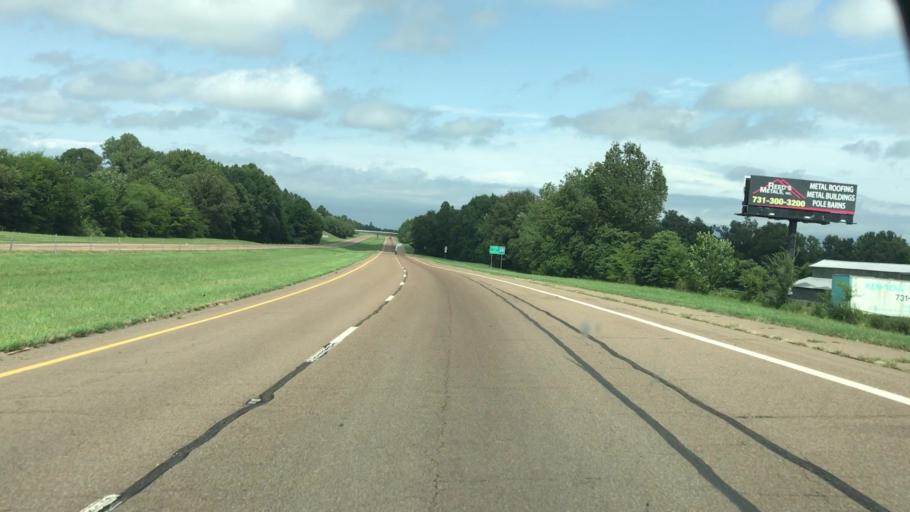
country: US
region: Tennessee
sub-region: Obion County
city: Union City
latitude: 36.4458
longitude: -89.0065
